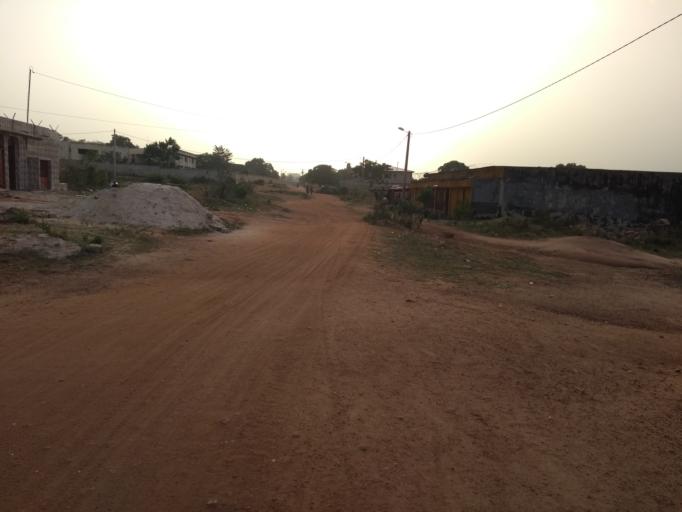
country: CI
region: Vallee du Bandama
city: Bouake
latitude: 7.7051
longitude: -5.0336
